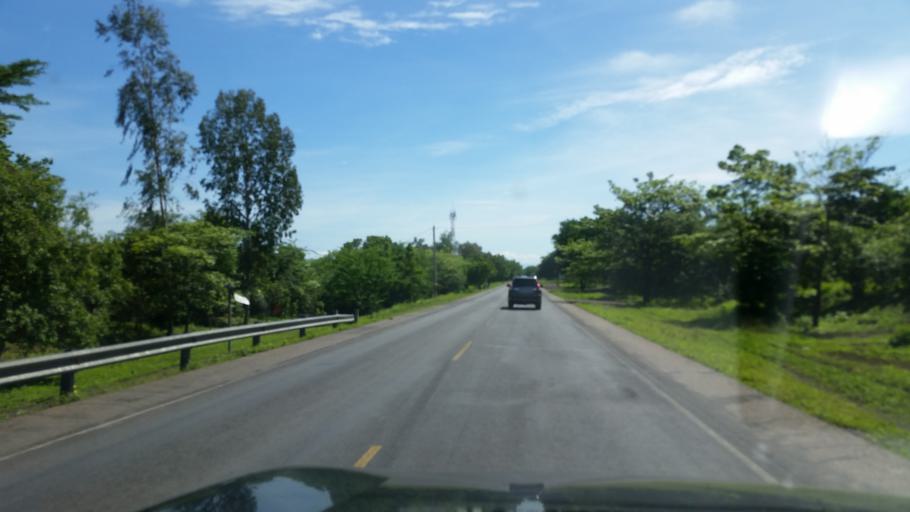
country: NI
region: Chinandega
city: Puerto Morazan
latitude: 12.7626
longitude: -87.0610
